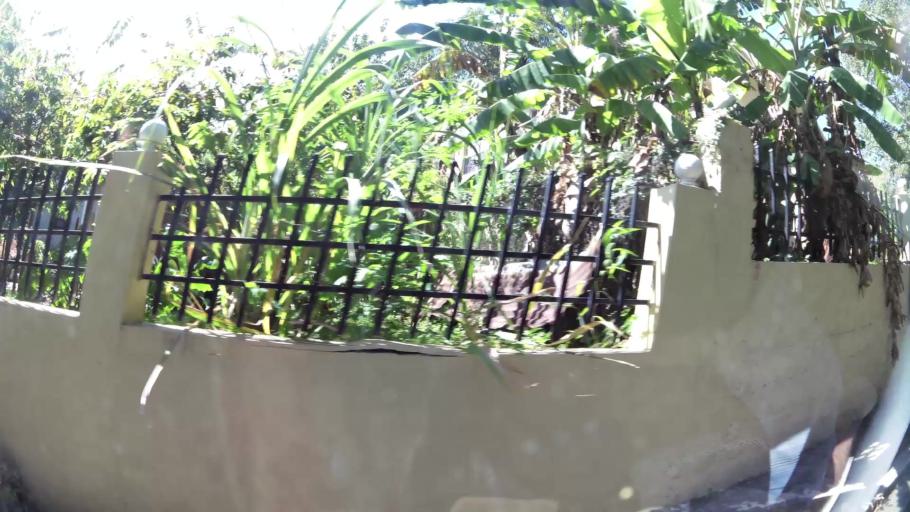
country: VG
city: Road Town
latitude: 18.4337
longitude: -64.6268
